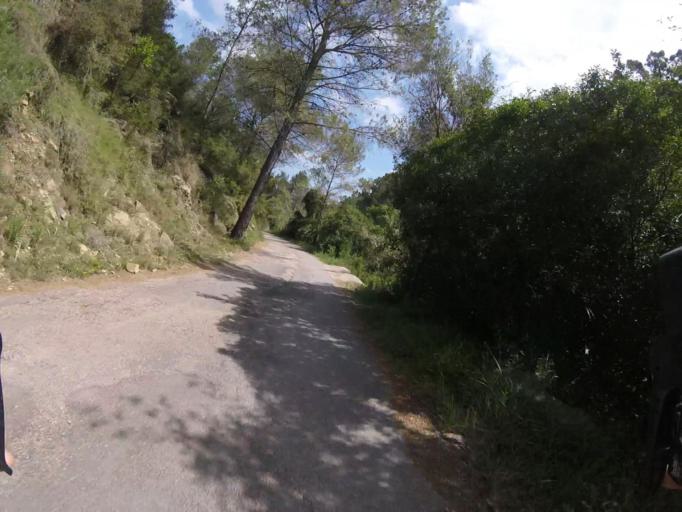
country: ES
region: Valencia
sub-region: Provincia de Castello
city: Cabanes
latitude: 40.1079
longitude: 0.0414
